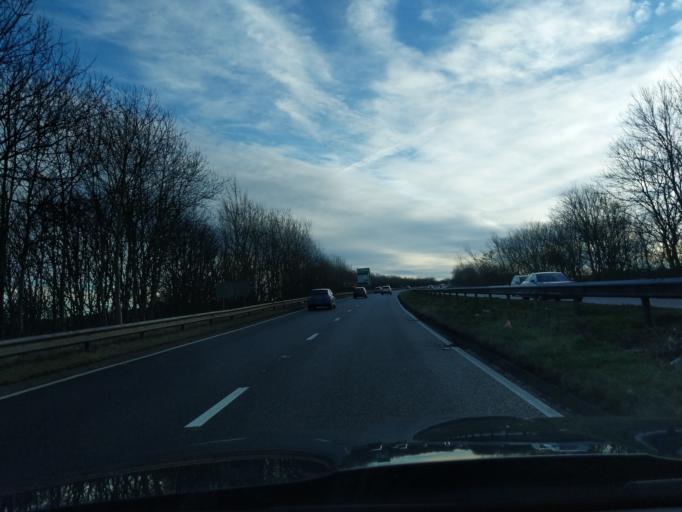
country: GB
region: England
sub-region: Northumberland
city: Seghill
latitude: 55.0515
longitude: -1.5560
